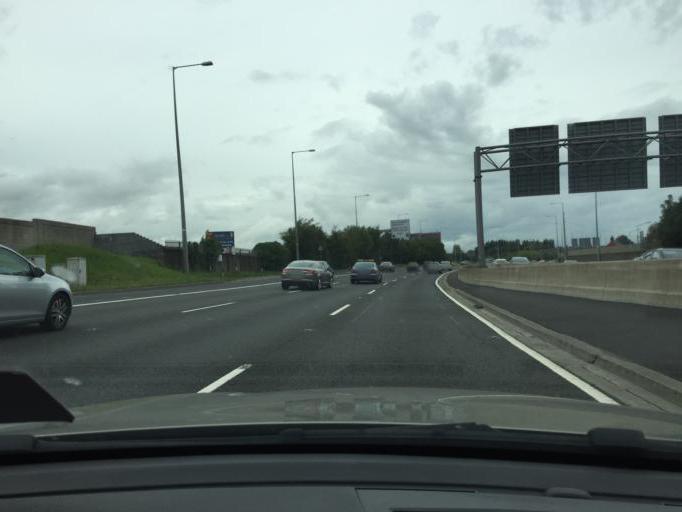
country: IE
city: Palmerstown
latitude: 53.3555
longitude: -6.3948
